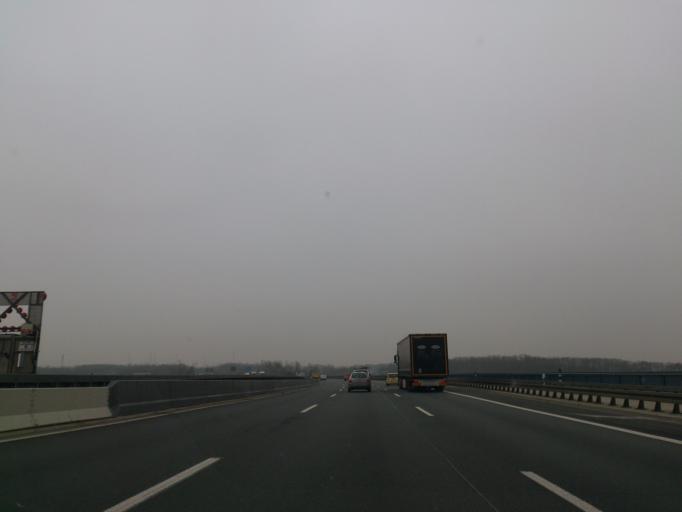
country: DE
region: North Rhine-Westphalia
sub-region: Regierungsbezirk Dusseldorf
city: Dusseldorf
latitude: 51.1815
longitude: 6.7741
